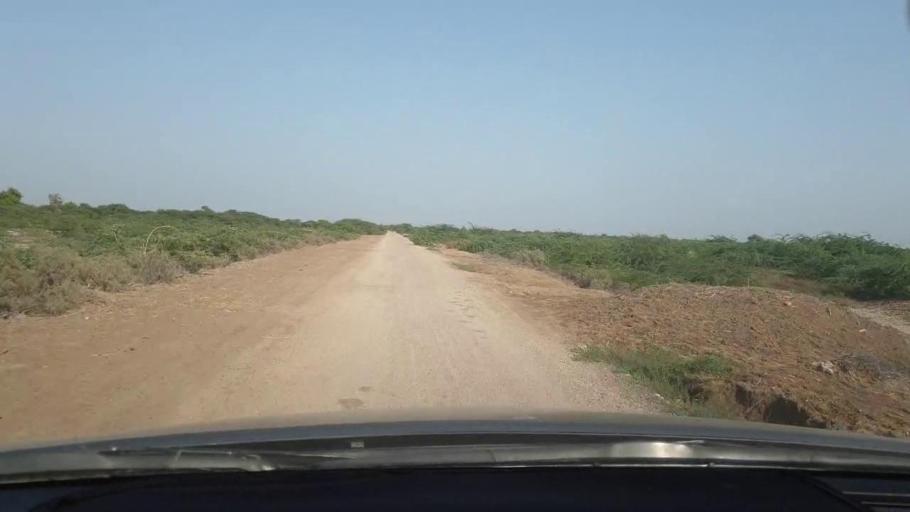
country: PK
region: Sindh
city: Naukot
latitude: 24.7780
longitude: 69.2843
